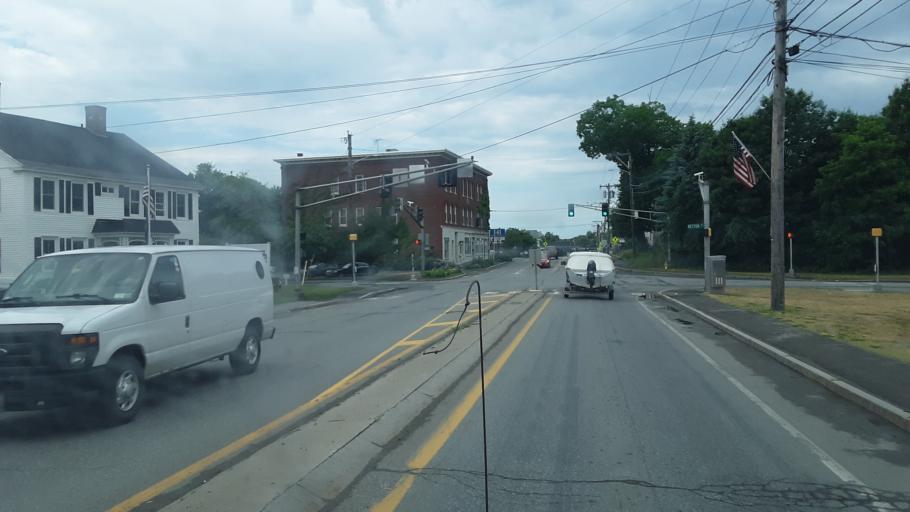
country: US
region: Maine
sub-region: Penobscot County
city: Brewer
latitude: 44.7965
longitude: -68.7627
